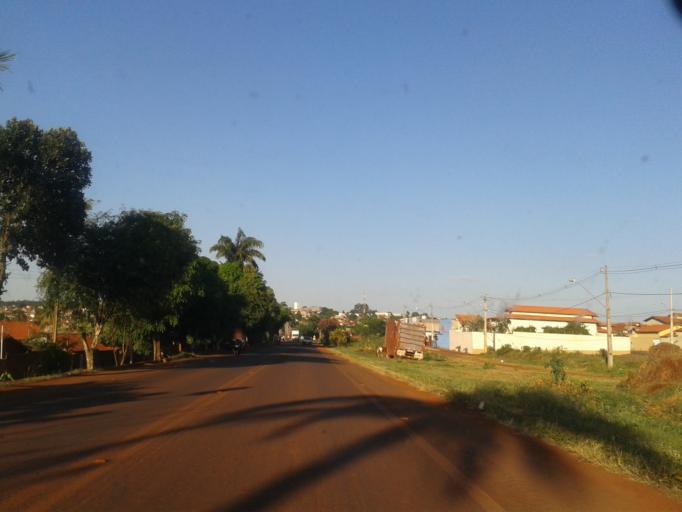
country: BR
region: Minas Gerais
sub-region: Capinopolis
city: Capinopolis
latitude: -18.6869
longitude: -49.5786
